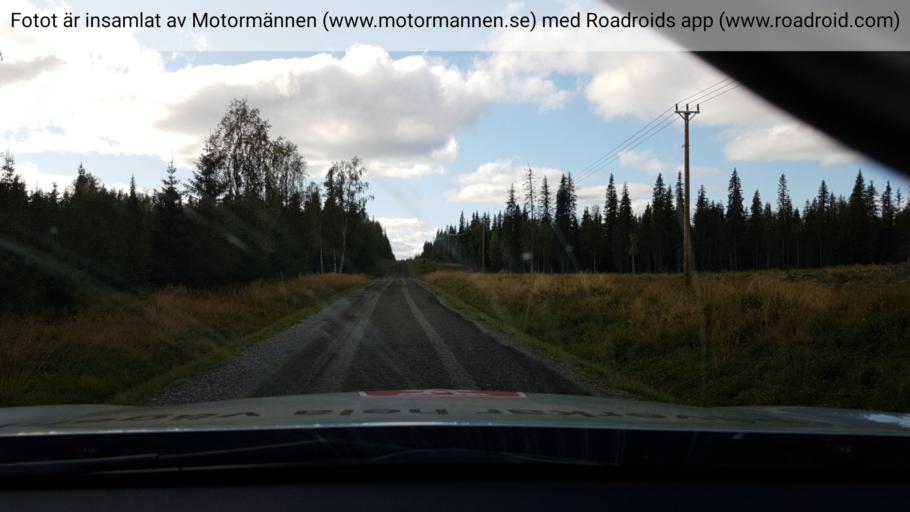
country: SE
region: Vaesterbotten
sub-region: Mala Kommun
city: Mala
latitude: 65.4950
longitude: 18.2833
